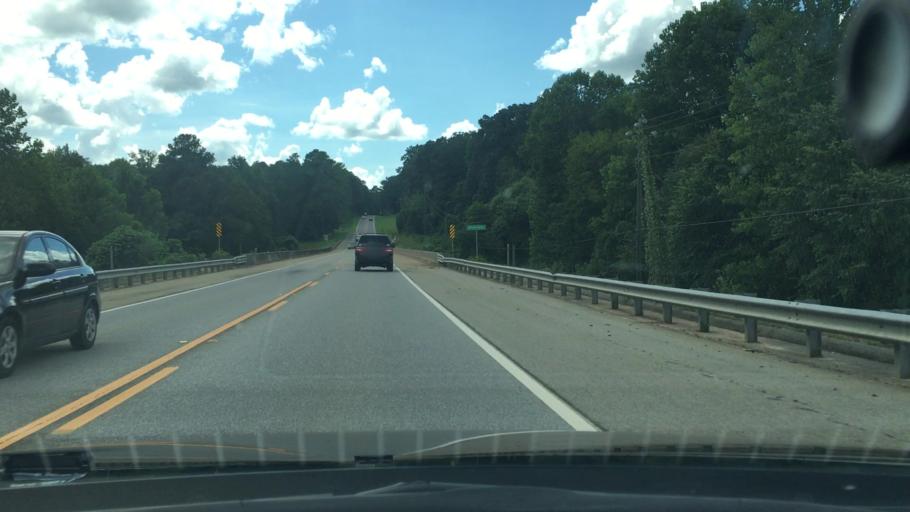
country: US
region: Georgia
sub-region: Putnam County
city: Eatonton
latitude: 33.3144
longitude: -83.4356
